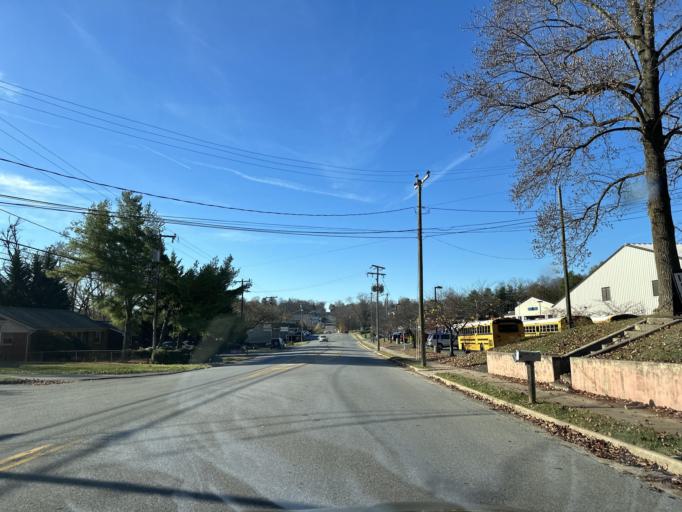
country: US
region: Virginia
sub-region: City of Staunton
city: Staunton
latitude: 38.1608
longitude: -79.0612
